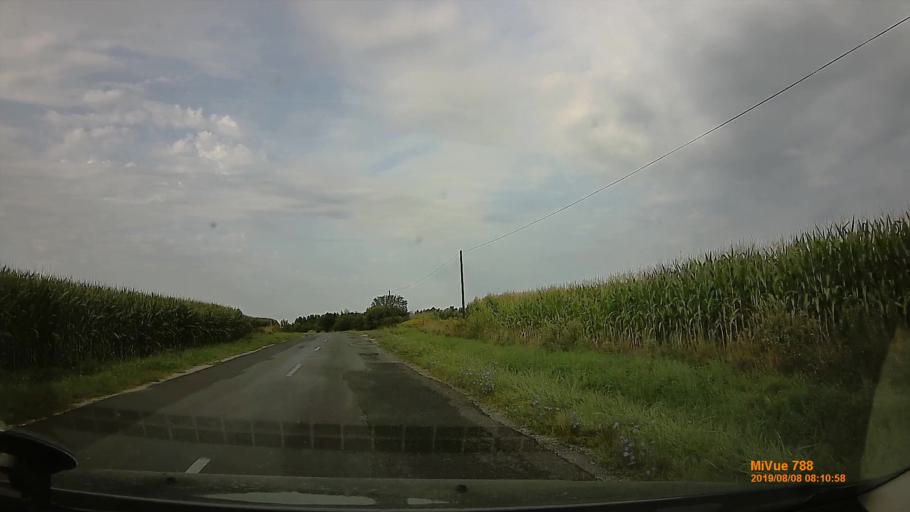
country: HU
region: Zala
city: Murakeresztur
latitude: 46.4268
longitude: 16.8853
